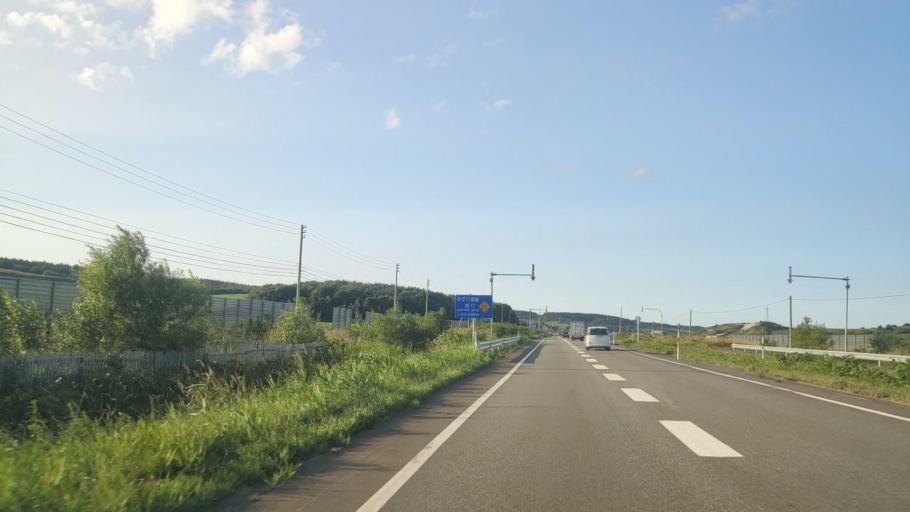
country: JP
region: Hokkaido
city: Wakkanai
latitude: 45.3218
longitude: 141.7193
